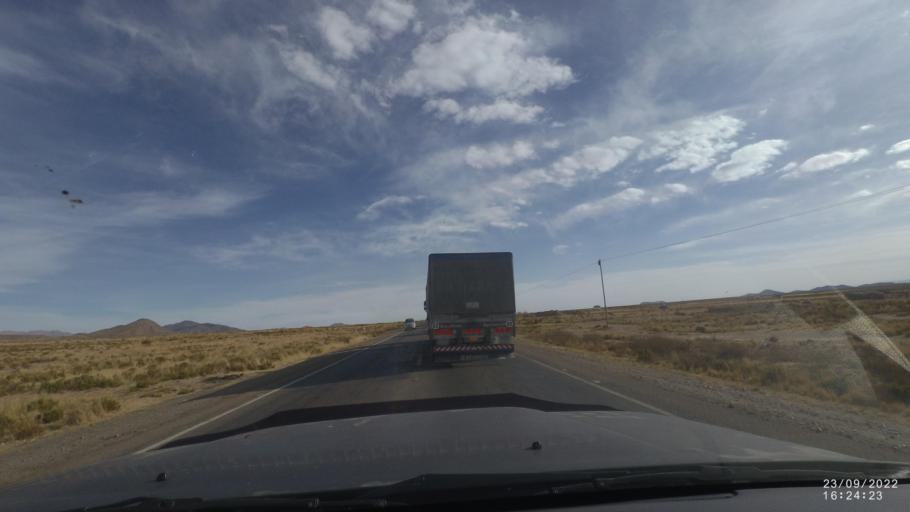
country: BO
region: Oruro
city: Machacamarca
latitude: -18.0826
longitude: -67.0081
